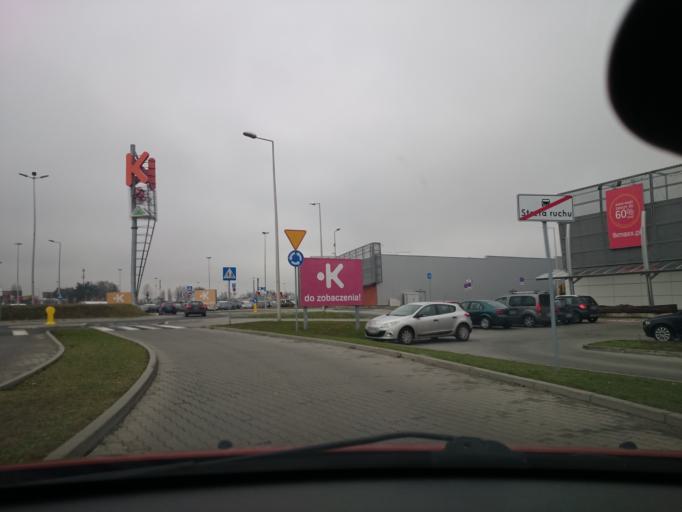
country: PL
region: Opole Voivodeship
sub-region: Powiat opolski
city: Chmielowice
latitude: 50.6808
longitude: 17.8809
